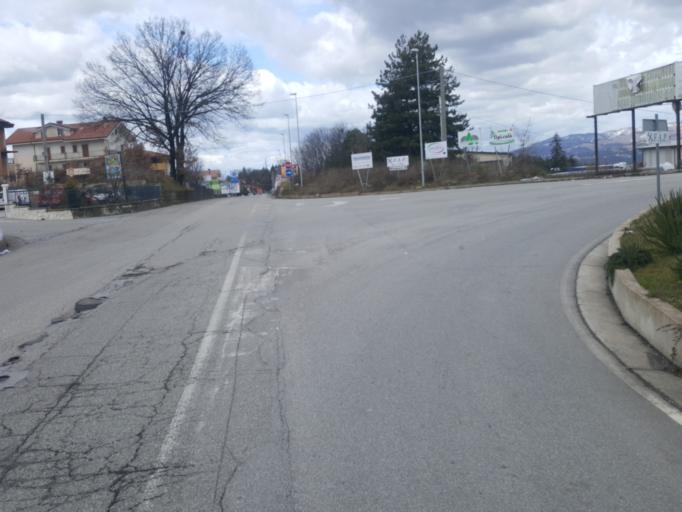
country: IT
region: Calabria
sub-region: Provincia di Cosenza
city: Piane Crati
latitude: 39.2160
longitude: 16.3075
